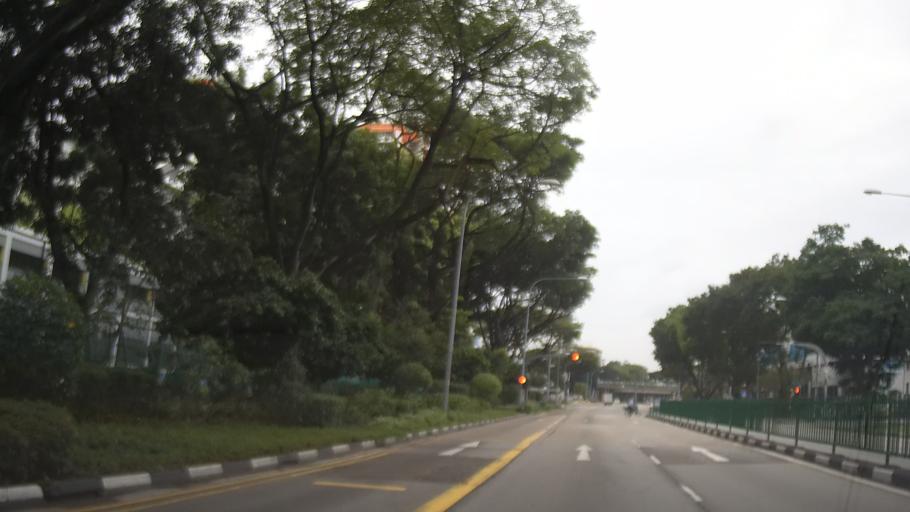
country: SG
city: Singapore
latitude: 1.3248
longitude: 103.8810
